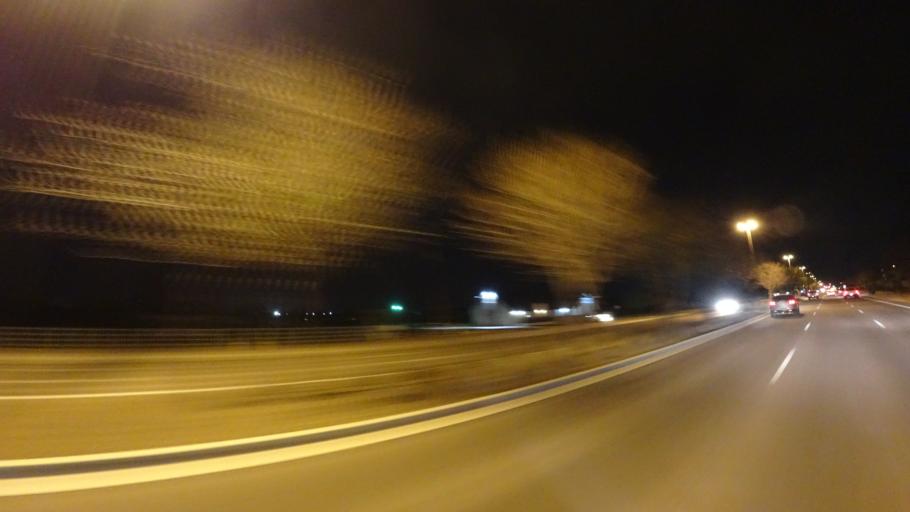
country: US
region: Arizona
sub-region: Maricopa County
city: Gilbert
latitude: 33.3287
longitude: -111.7557
